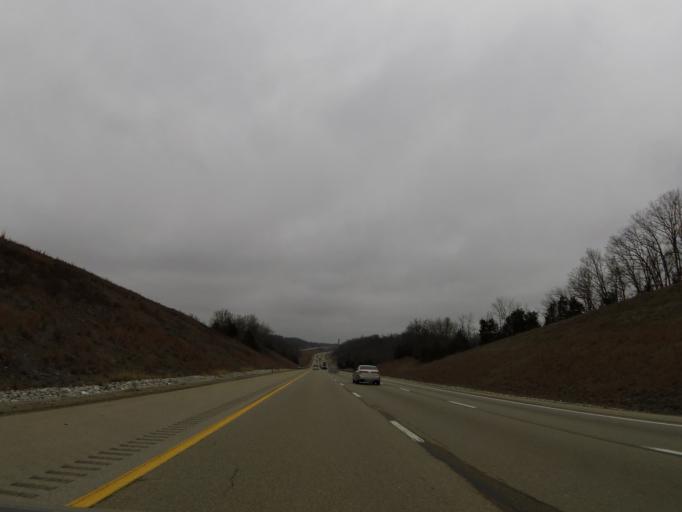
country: US
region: Kentucky
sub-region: Grant County
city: Williamstown
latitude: 38.5465
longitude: -84.5978
